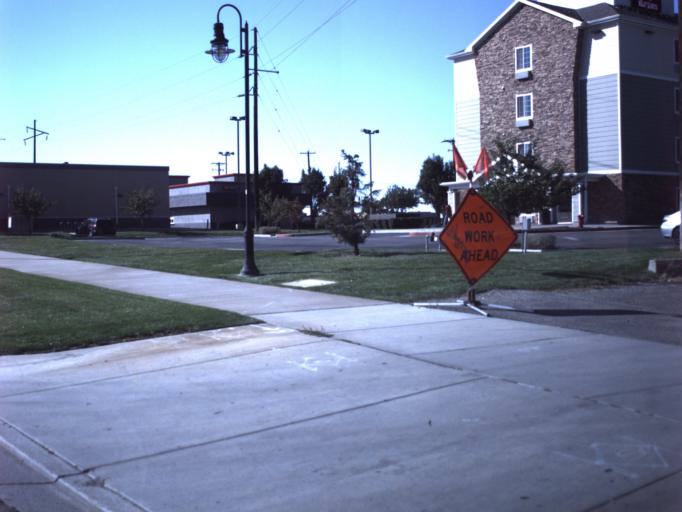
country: US
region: Utah
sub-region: Salt Lake County
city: Taylorsville
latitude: 40.6967
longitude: -111.9372
